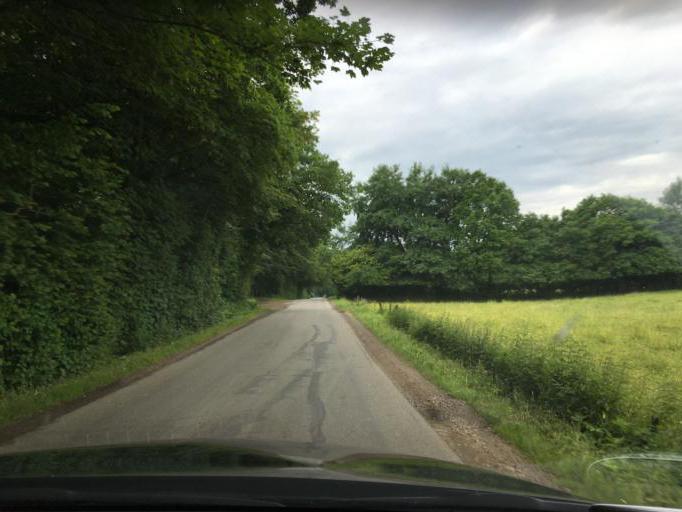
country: DK
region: South Denmark
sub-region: Vejle Kommune
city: Vejle
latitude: 55.6162
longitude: 9.5050
